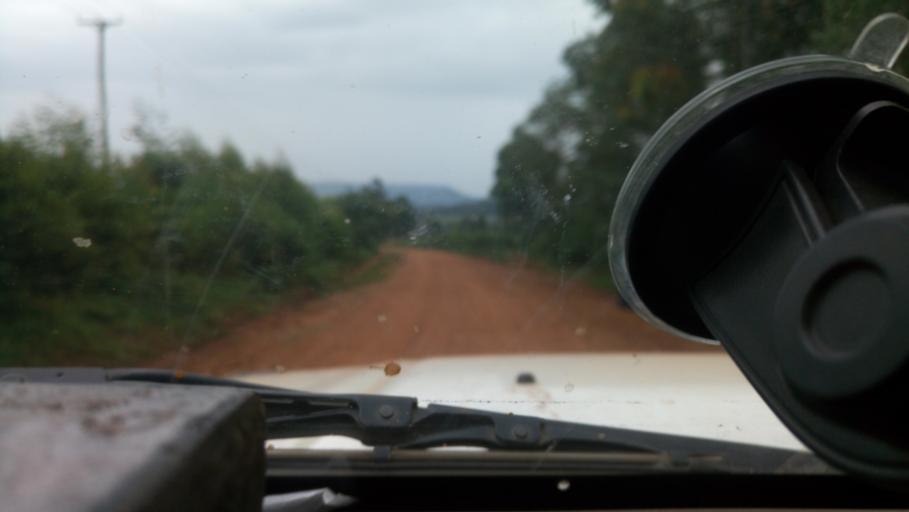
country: KE
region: Kisii
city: Ogembo
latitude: -0.8879
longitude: 34.6113
